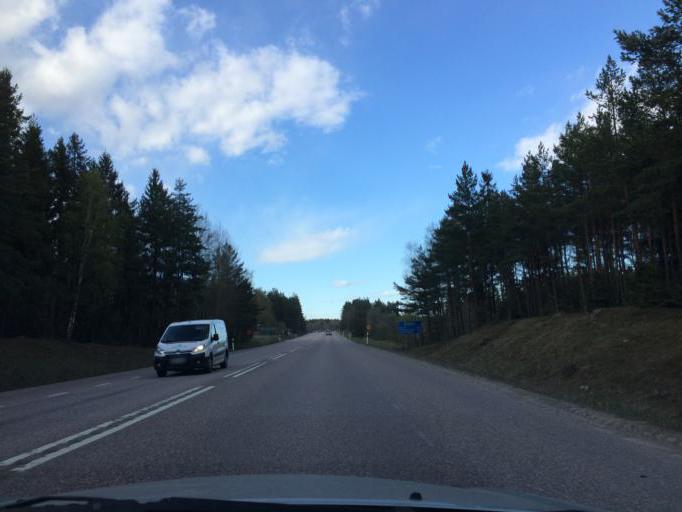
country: SE
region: Vaestmanland
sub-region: Hallstahammars Kommun
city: Kolback
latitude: 59.5683
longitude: 16.3499
